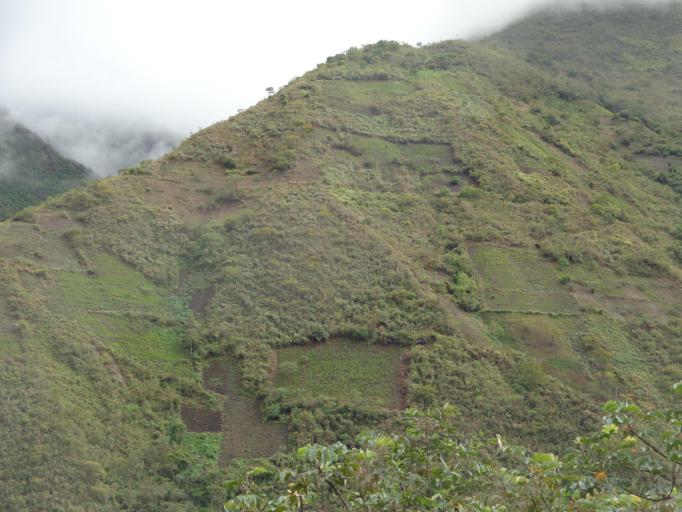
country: BO
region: La Paz
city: Coripata
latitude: -16.4021
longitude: -67.6627
